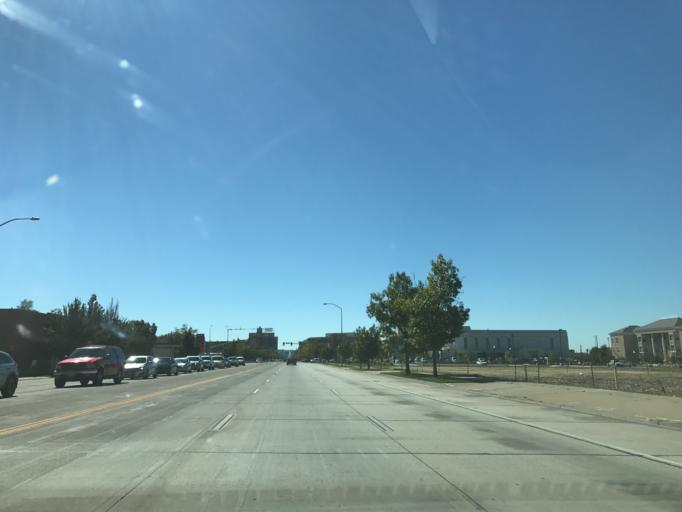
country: US
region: Utah
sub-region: Weber County
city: Ogden
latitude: 41.2309
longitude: -111.9704
